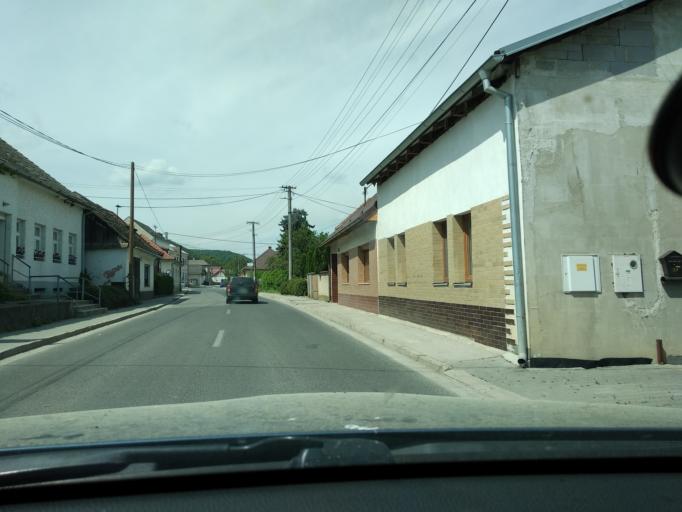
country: SK
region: Trenciansky
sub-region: Okres Nove Mesto nad Vahom
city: Nove Mesto nad Vahom
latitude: 48.8276
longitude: 17.8394
